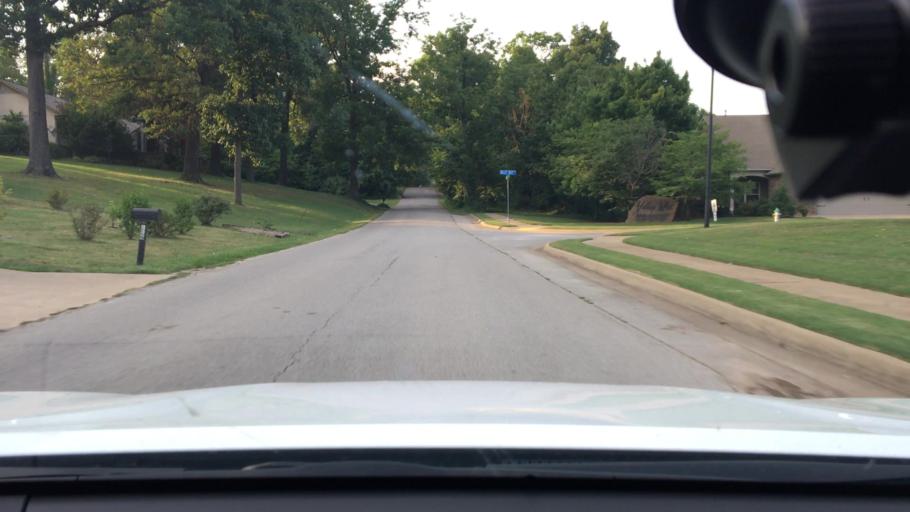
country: US
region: Arkansas
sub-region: Benton County
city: Rogers
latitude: 36.3358
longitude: -94.1626
